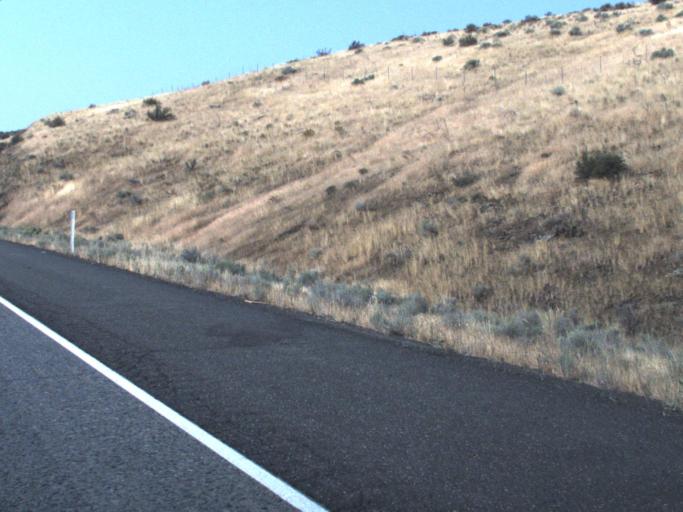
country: US
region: Washington
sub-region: Yakima County
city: Terrace Heights
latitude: 46.7845
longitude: -120.3706
